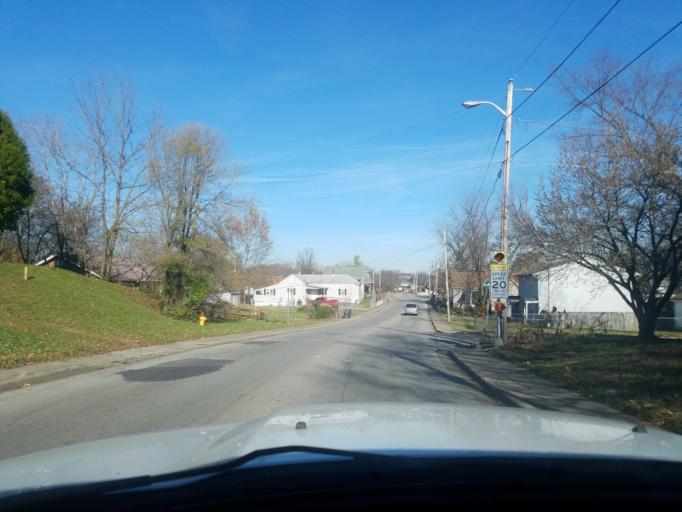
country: US
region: Indiana
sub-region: Floyd County
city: New Albany
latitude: 38.2929
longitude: -85.8265
